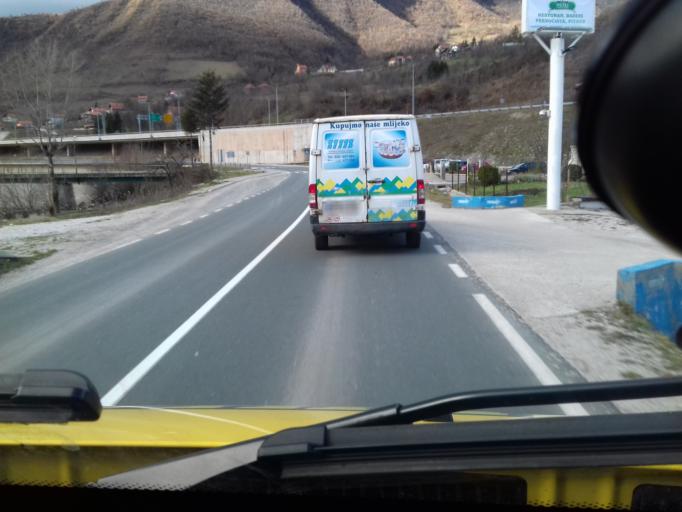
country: BA
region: Federation of Bosnia and Herzegovina
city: Kacuni
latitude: 44.1338
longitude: 17.9943
